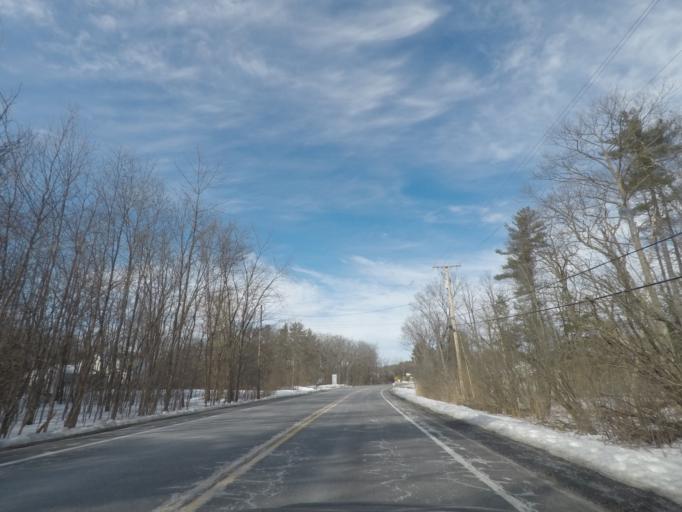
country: US
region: New York
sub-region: Albany County
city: Voorheesville
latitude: 42.6562
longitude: -73.9393
